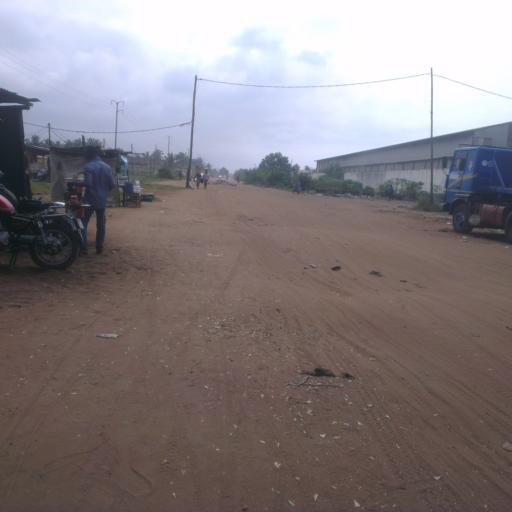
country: TG
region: Maritime
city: Lome
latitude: 6.1619
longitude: 1.2961
